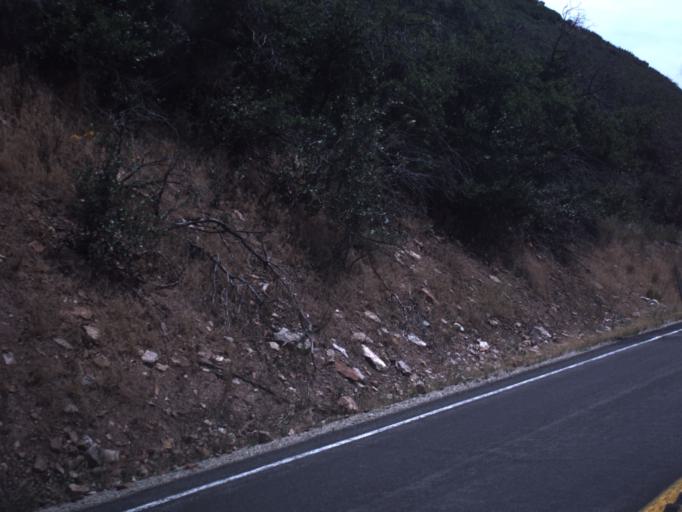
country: US
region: Utah
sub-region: Summit County
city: Francis
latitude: 40.5587
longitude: -111.1725
